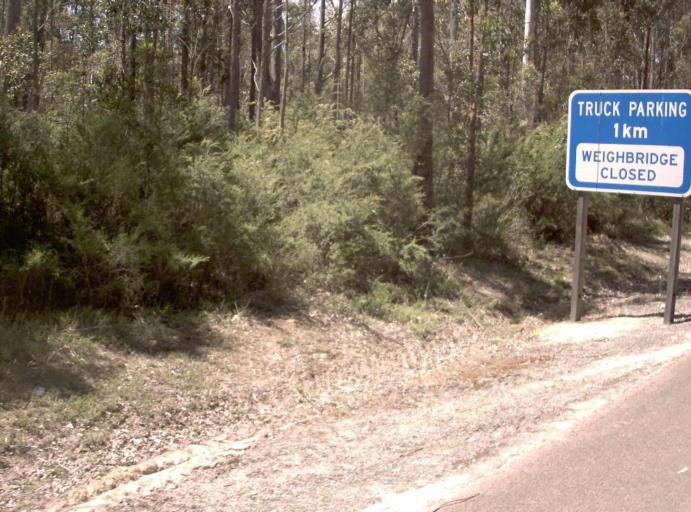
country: AU
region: New South Wales
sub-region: Bombala
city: Bombala
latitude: -37.5665
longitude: 149.0984
